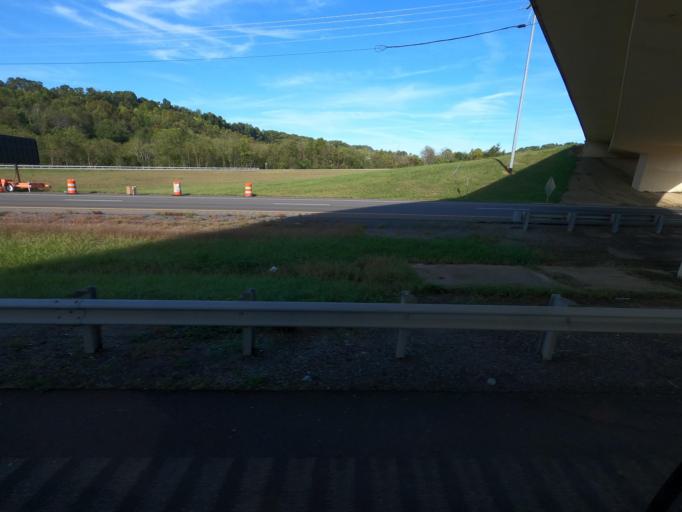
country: US
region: Tennessee
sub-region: Washington County
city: Fall Branch
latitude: 36.4028
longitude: -82.6176
